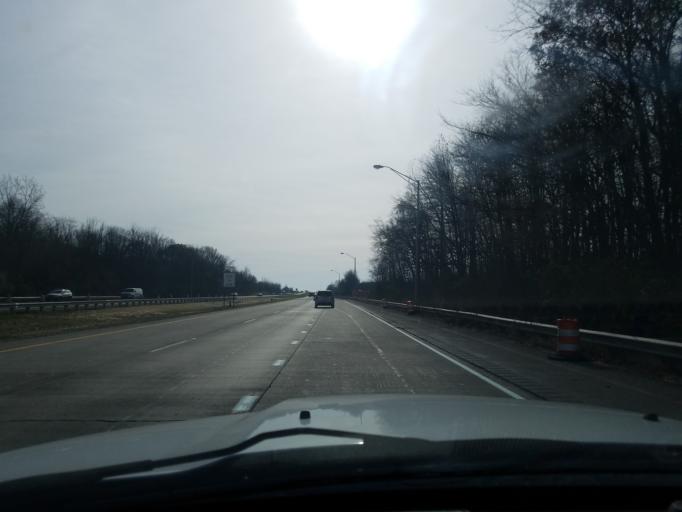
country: US
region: Indiana
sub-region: Delaware County
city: Yorktown
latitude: 40.2158
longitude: -85.5611
